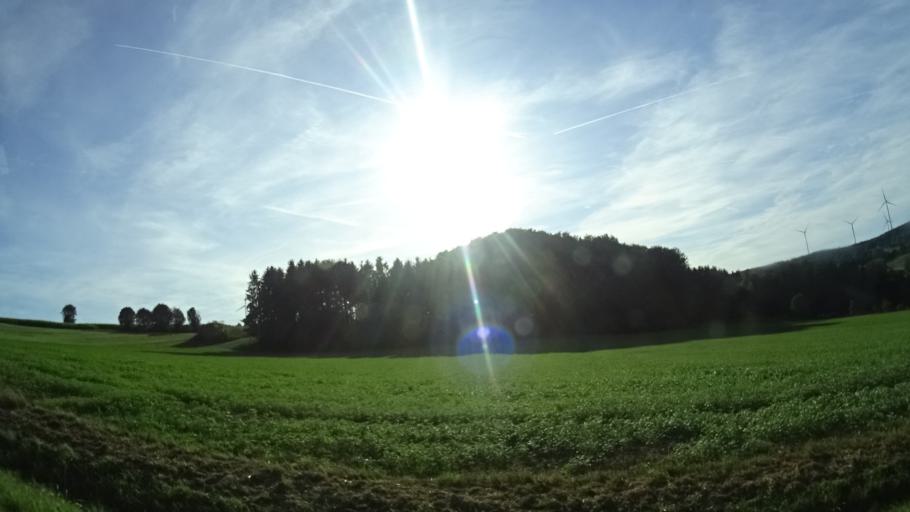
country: DE
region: Hesse
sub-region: Regierungsbezirk Kassel
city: Flieden
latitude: 50.4206
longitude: 9.5127
